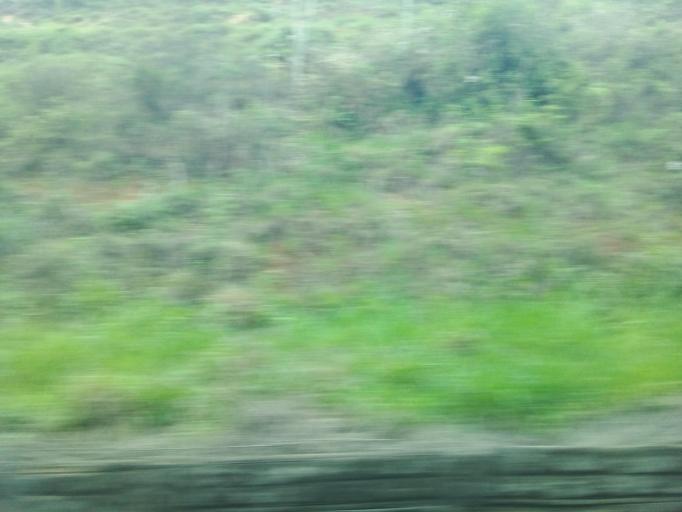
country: BR
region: Minas Gerais
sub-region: Belo Oriente
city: Belo Oriente
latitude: -19.2173
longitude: -42.2984
